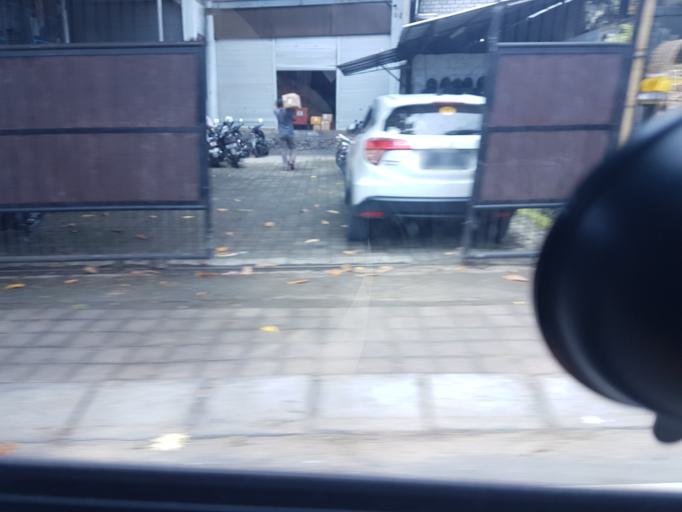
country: ID
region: Bali
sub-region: Kabupaten Gianyar
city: Ubud
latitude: -8.5372
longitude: 115.2728
